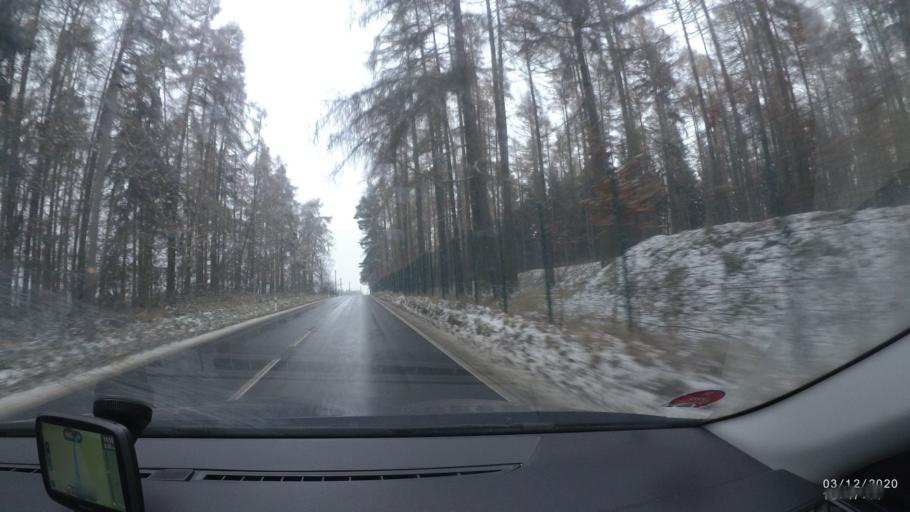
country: CZ
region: Central Bohemia
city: Nove Straseci
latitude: 50.1678
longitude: 13.8987
